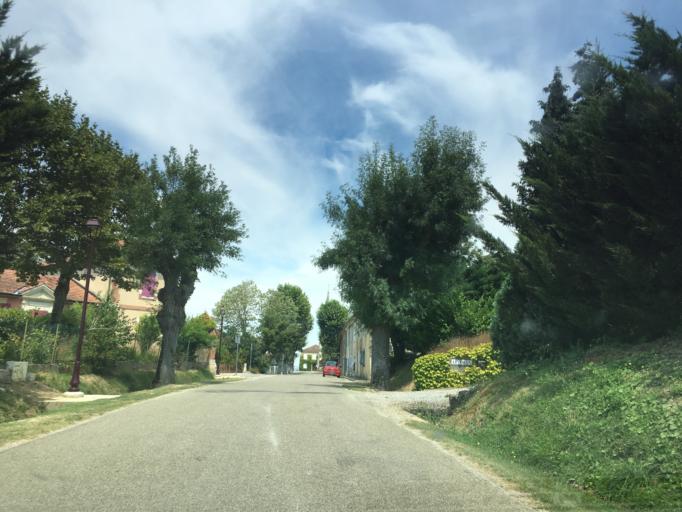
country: FR
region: Midi-Pyrenees
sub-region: Departement du Gers
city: Jegun
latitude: 43.8129
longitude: 0.5497
